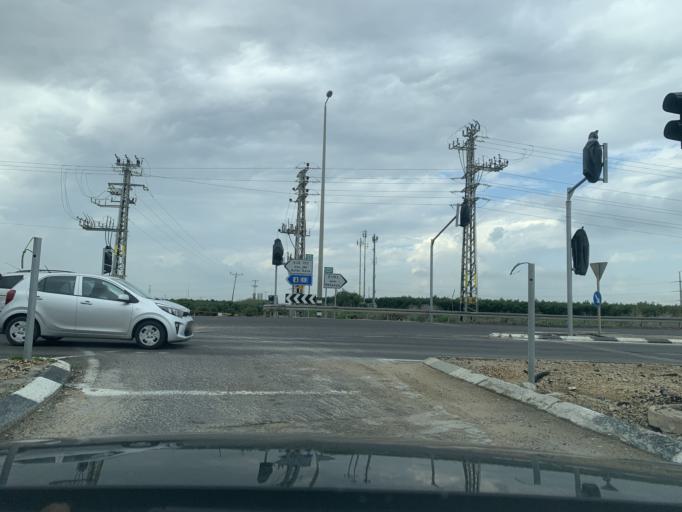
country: PS
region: West Bank
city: Qalqilyah
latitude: 32.2096
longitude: 34.9735
